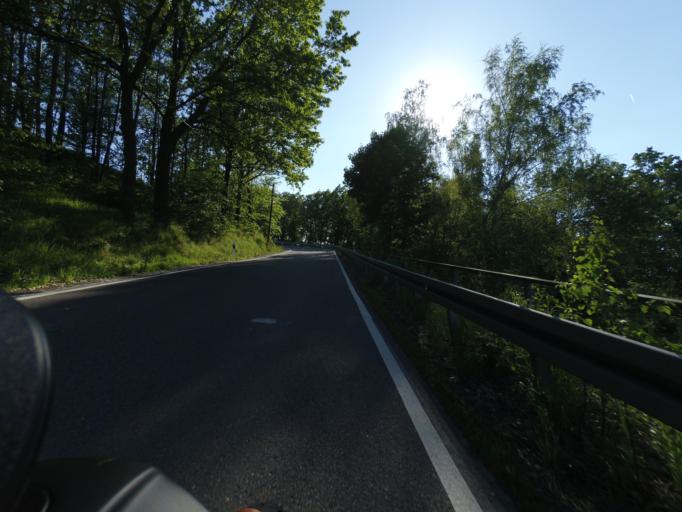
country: DE
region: Saxony
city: Rabenau
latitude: 50.9687
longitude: 13.6556
